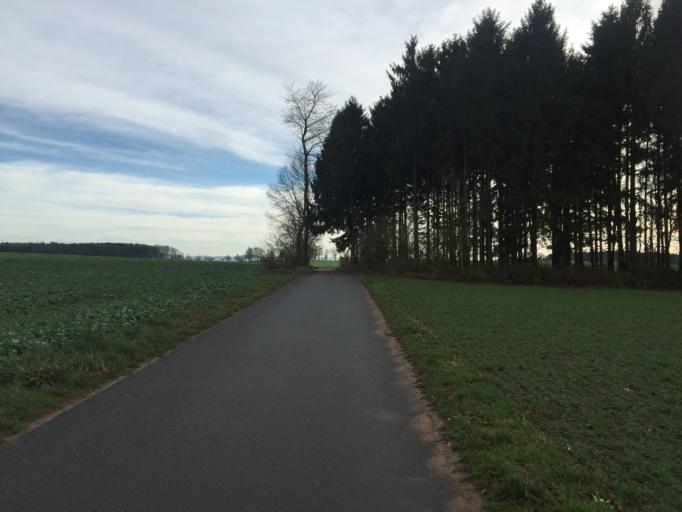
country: DE
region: Hesse
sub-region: Regierungsbezirk Darmstadt
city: Erbach
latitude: 49.6804
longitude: 8.9372
